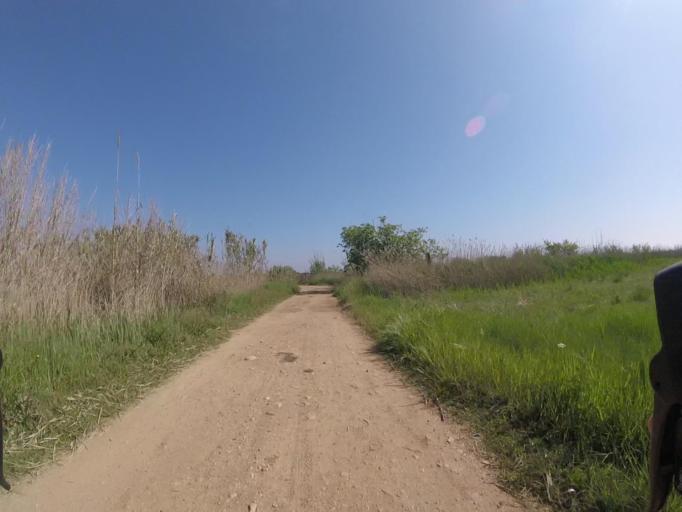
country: ES
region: Valencia
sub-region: Provincia de Castello
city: Orpesa/Oropesa del Mar
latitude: 40.1568
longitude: 0.1720
